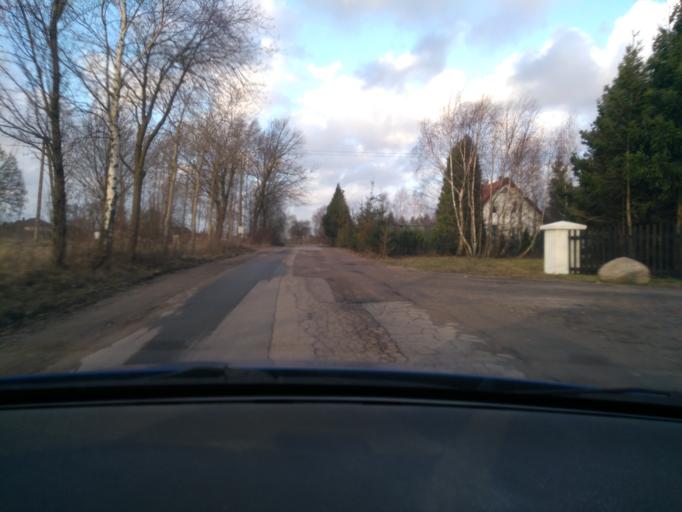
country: PL
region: Pomeranian Voivodeship
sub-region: Powiat kartuski
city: Kartuzy
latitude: 54.3939
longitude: 18.2229
